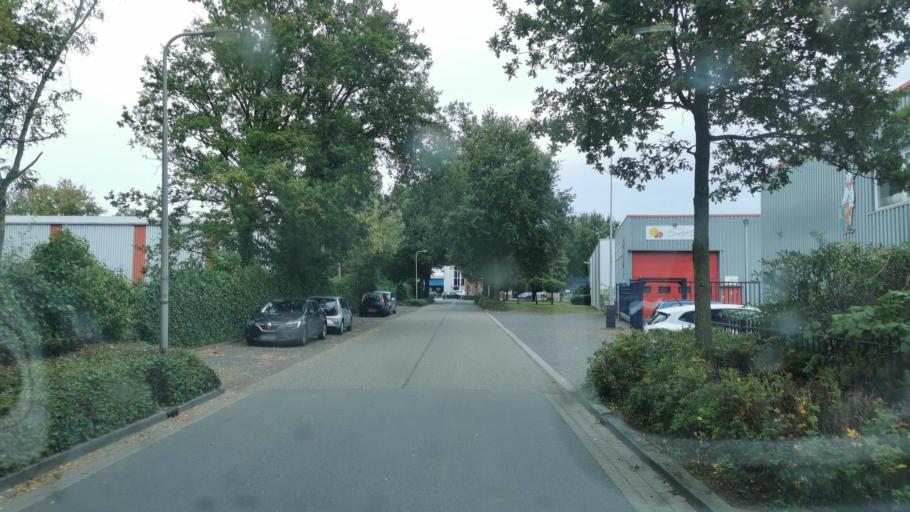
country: NL
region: Overijssel
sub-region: Gemeente Losser
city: Losser
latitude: 52.2494
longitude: 7.0139
